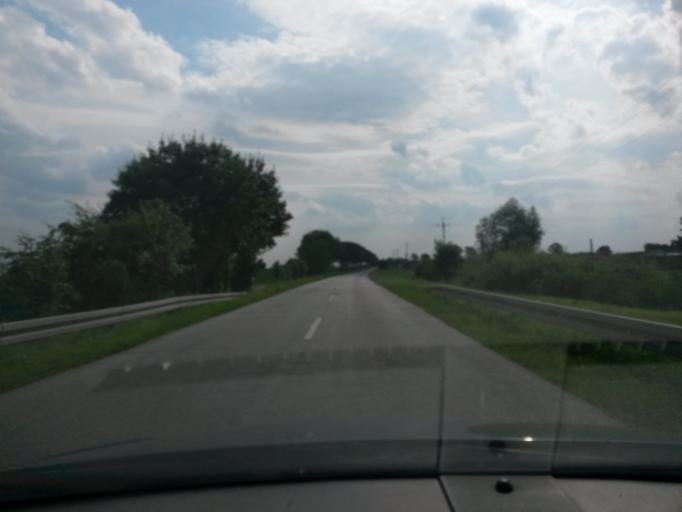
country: PL
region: Greater Poland Voivodeship
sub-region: Powiat poznanski
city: Kornik
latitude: 52.2918
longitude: 17.1185
